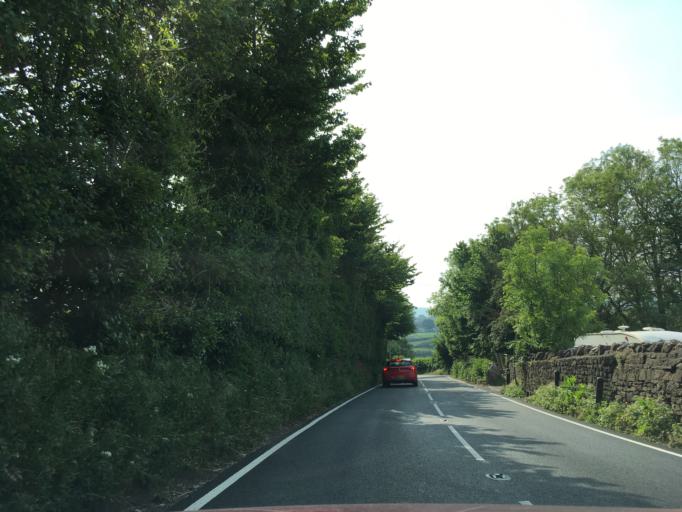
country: GB
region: England
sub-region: North Somerset
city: Nailsea
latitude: 51.4419
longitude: -2.7687
